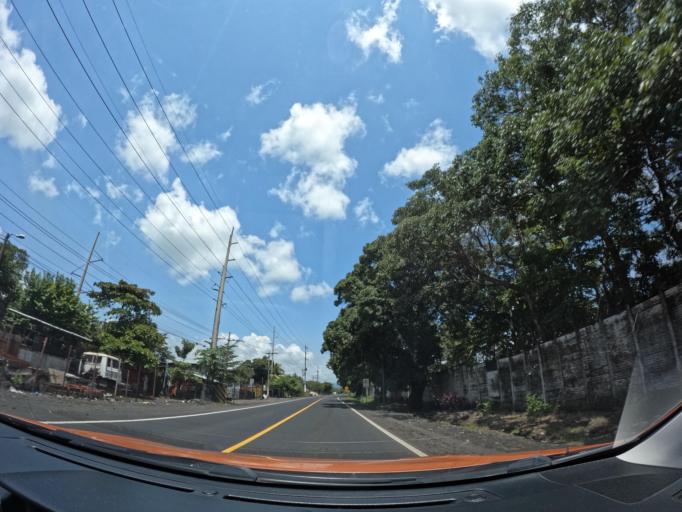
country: GT
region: Escuintla
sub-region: Municipio de Masagua
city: Masagua
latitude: 14.2358
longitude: -90.8204
